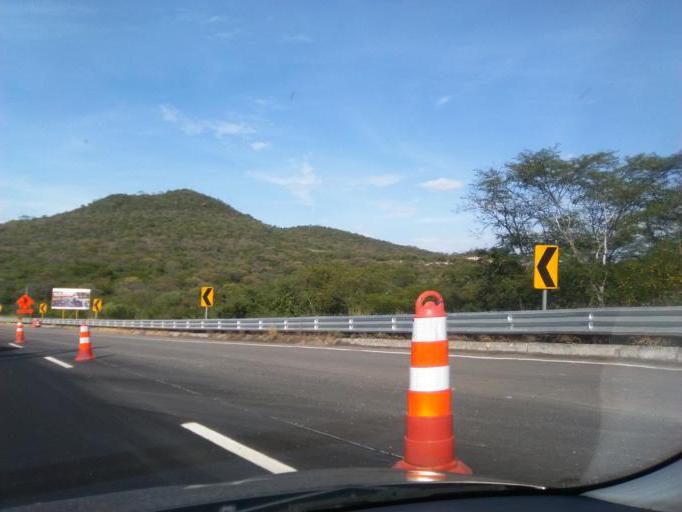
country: MX
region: Morelos
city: Tilzapotla
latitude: 18.4394
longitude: -99.1741
